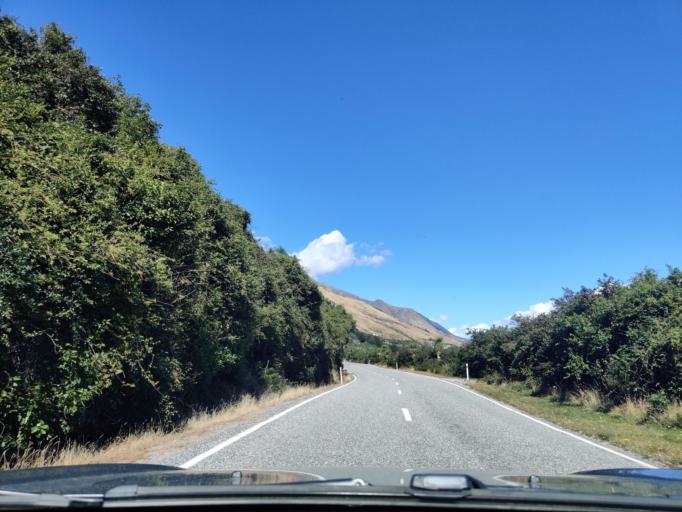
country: NZ
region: Otago
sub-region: Queenstown-Lakes District
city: Queenstown
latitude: -44.9472
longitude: 168.4340
